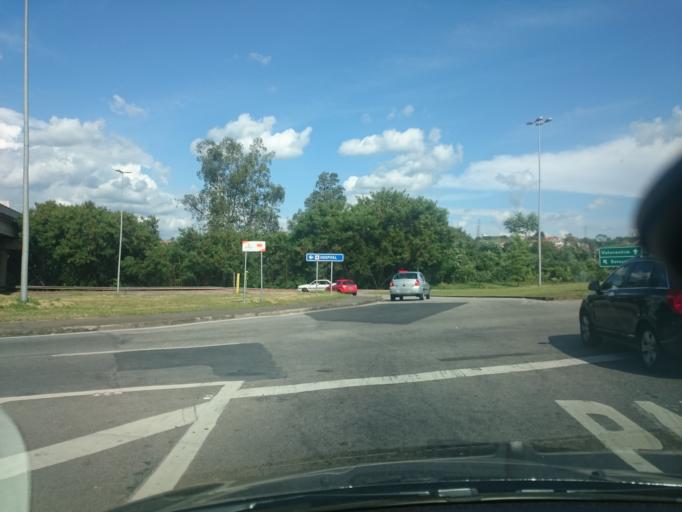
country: BR
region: Sao Paulo
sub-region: Votorantim
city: Votorantim
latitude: -23.5271
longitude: -47.4504
